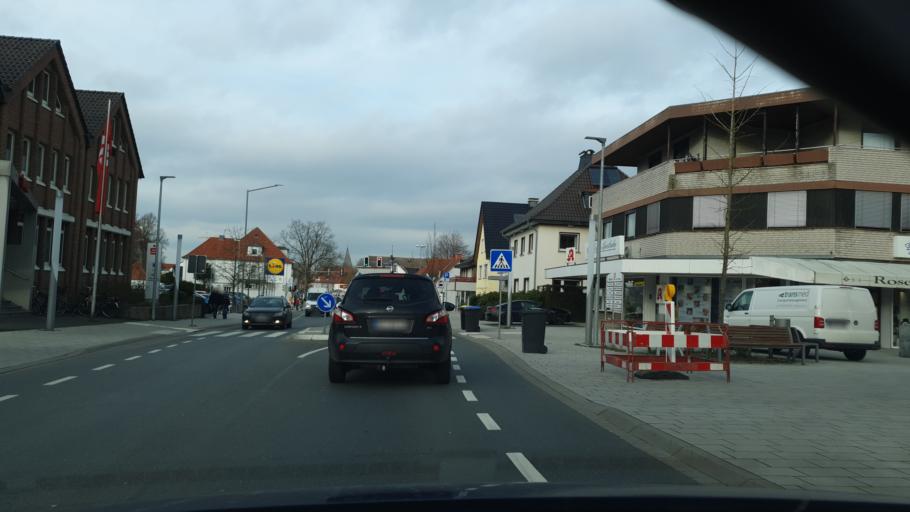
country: DE
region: North Rhine-Westphalia
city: Spenge
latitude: 52.1410
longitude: 8.4828
